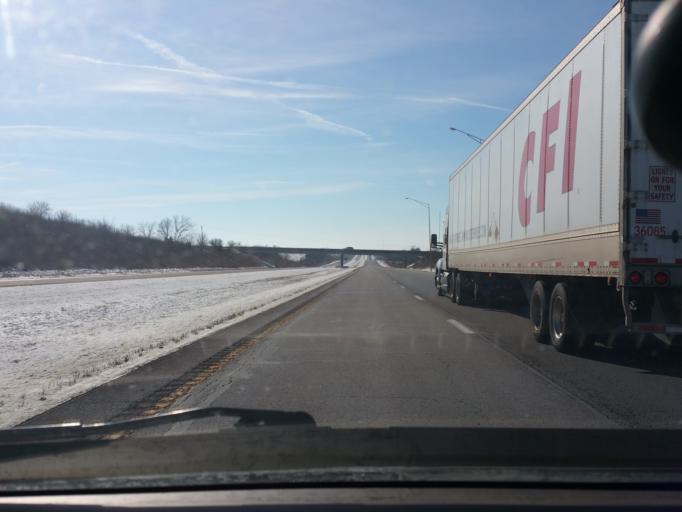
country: US
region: Iowa
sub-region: Decatur County
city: Lamoni
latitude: 40.5469
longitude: -93.9544
